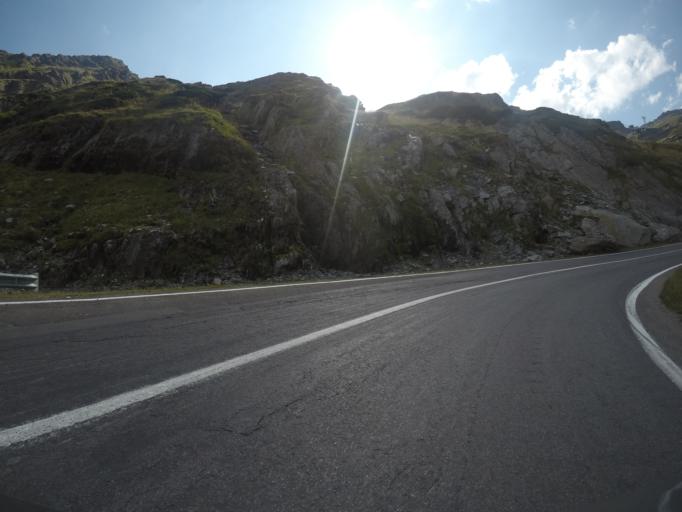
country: RO
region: Sibiu
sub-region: Comuna Cartisoara
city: Cartisoara
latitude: 45.6120
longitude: 24.6164
